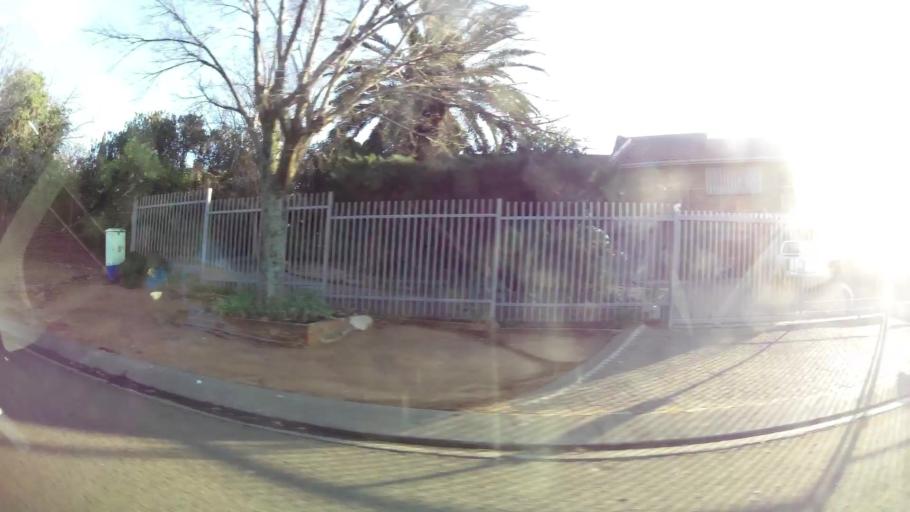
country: ZA
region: Orange Free State
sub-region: Mangaung Metropolitan Municipality
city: Bloemfontein
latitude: -29.1548
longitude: 26.1713
